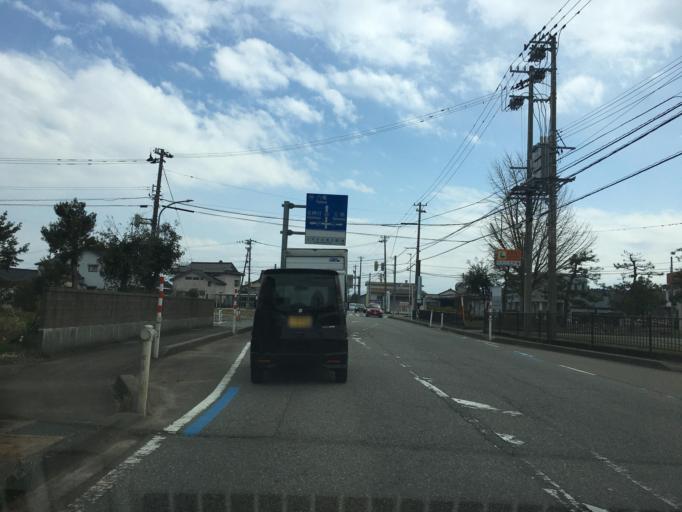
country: JP
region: Toyama
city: Kuragaki-kosugi
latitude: 36.6836
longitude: 137.1206
